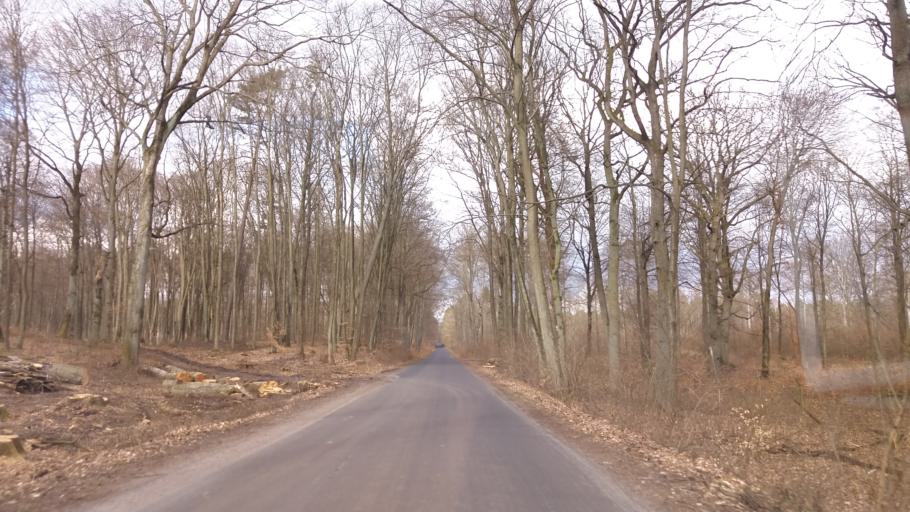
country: PL
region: West Pomeranian Voivodeship
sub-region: Powiat choszczenski
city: Recz
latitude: 53.1961
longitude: 15.6343
